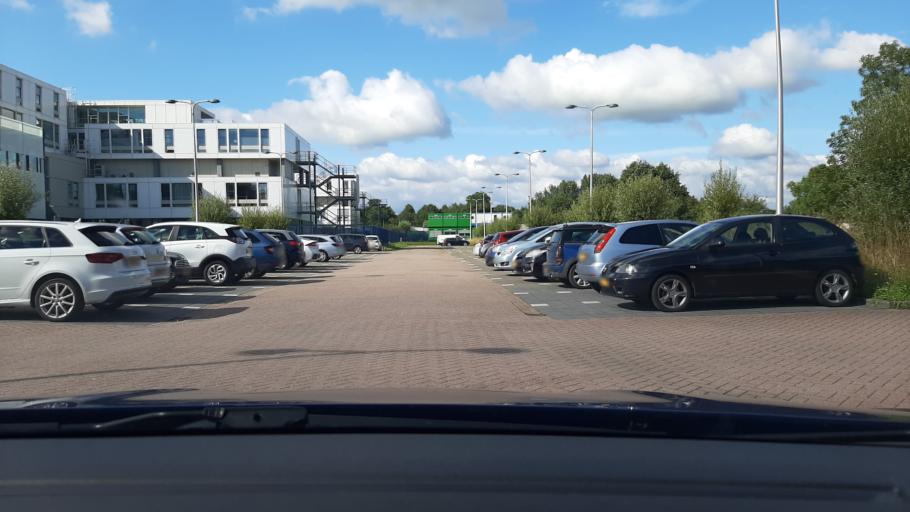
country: NL
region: North Holland
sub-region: Gemeente Purmerend
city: Purmerend
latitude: 52.5015
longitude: 4.9625
